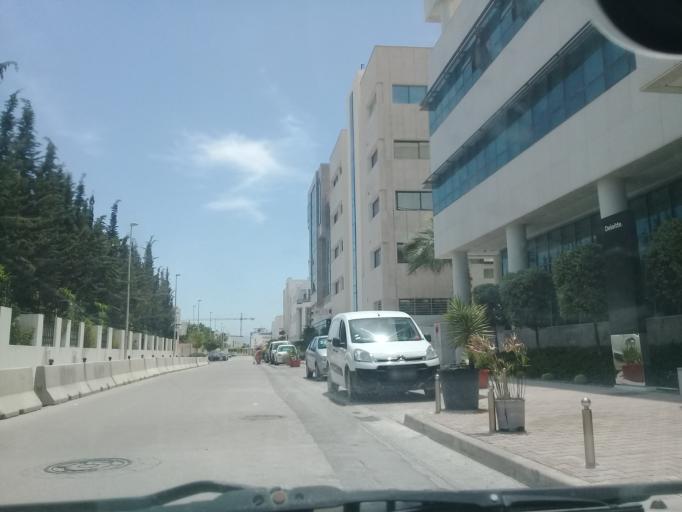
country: TN
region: Ariana
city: Ariana
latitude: 36.8363
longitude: 10.2306
